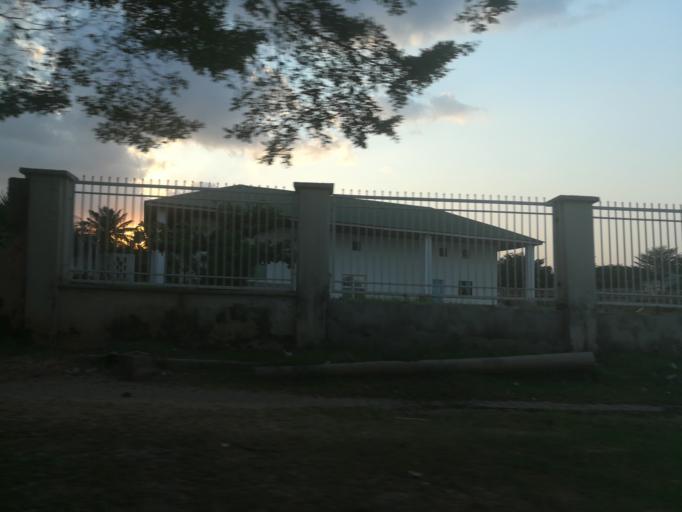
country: NG
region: Abuja Federal Capital Territory
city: Abuja
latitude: 9.0763
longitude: 7.4164
